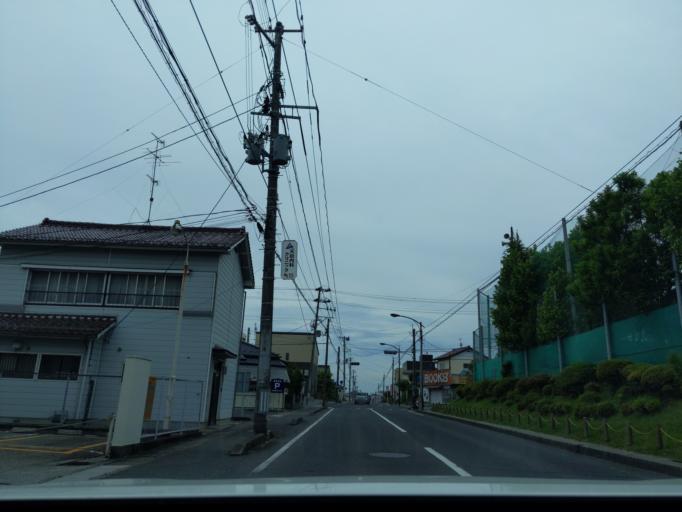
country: JP
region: Fukushima
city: Koriyama
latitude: 37.3859
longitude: 140.3704
